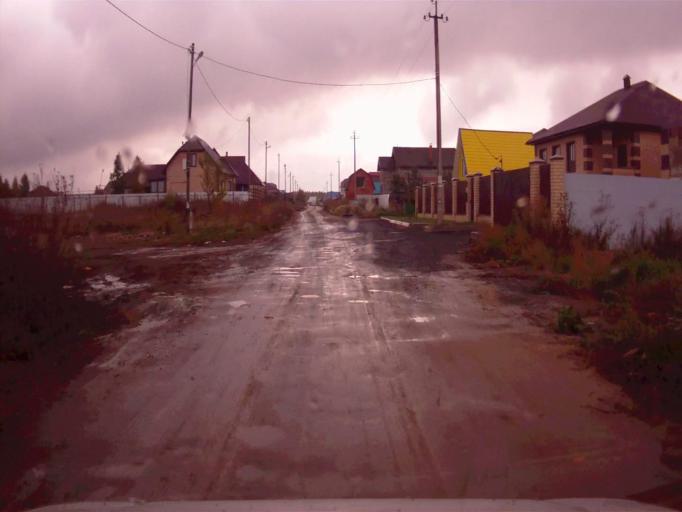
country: RU
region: Chelyabinsk
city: Dolgoderevenskoye
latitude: 55.3091
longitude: 61.3412
